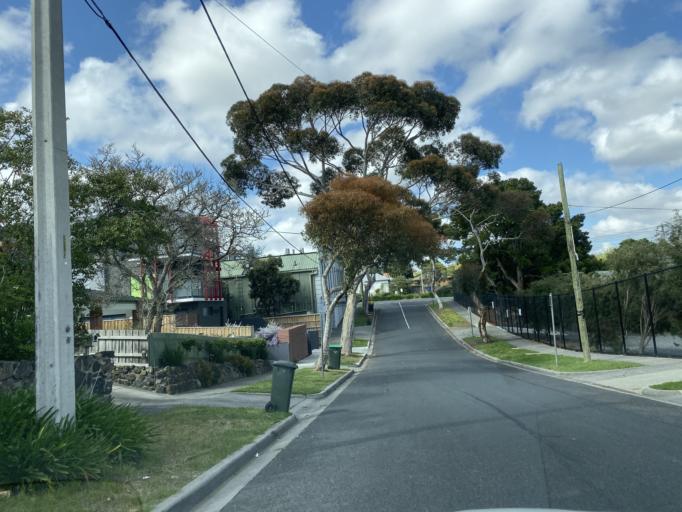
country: AU
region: Victoria
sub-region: Whitehorse
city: Burwood
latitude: -37.8494
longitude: 145.1177
